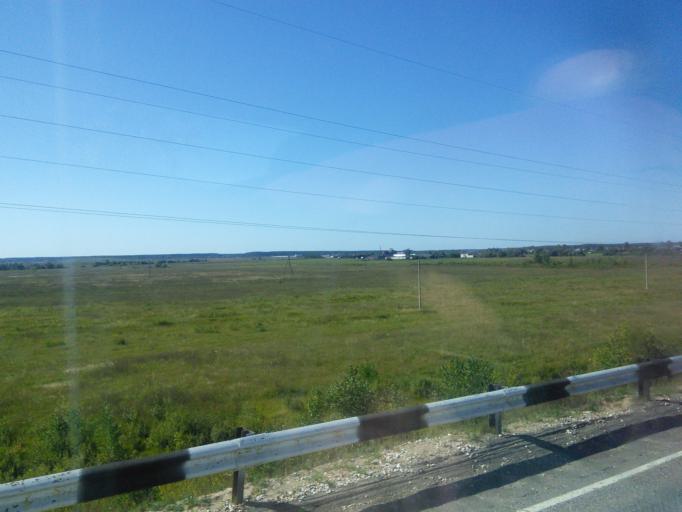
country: RU
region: Tverskaya
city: Kalyazin
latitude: 57.2333
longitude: 37.7888
